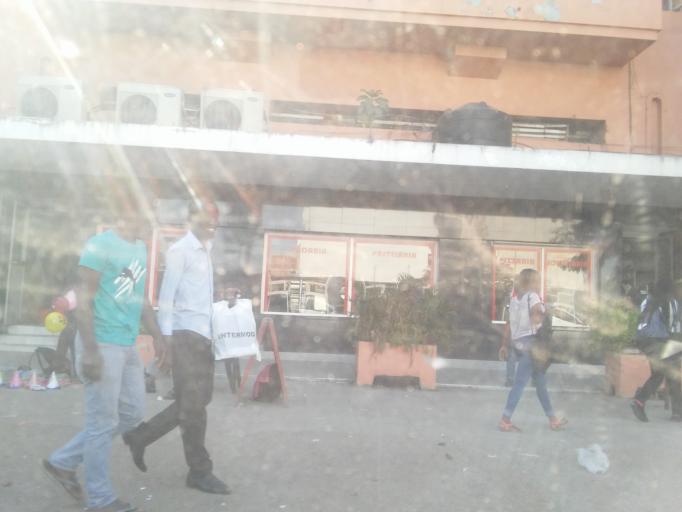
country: MZ
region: Maputo City
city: Maputo
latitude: -25.9636
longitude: 32.5702
